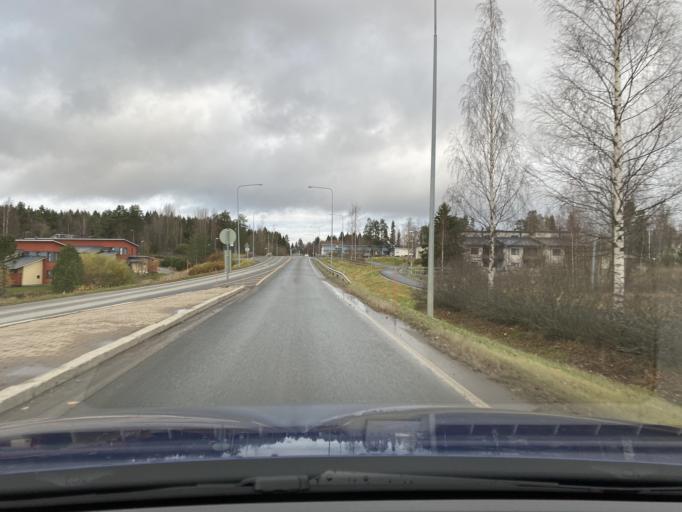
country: FI
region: Pirkanmaa
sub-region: Tampere
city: Lempaeaelae
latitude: 61.3819
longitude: 23.7799
